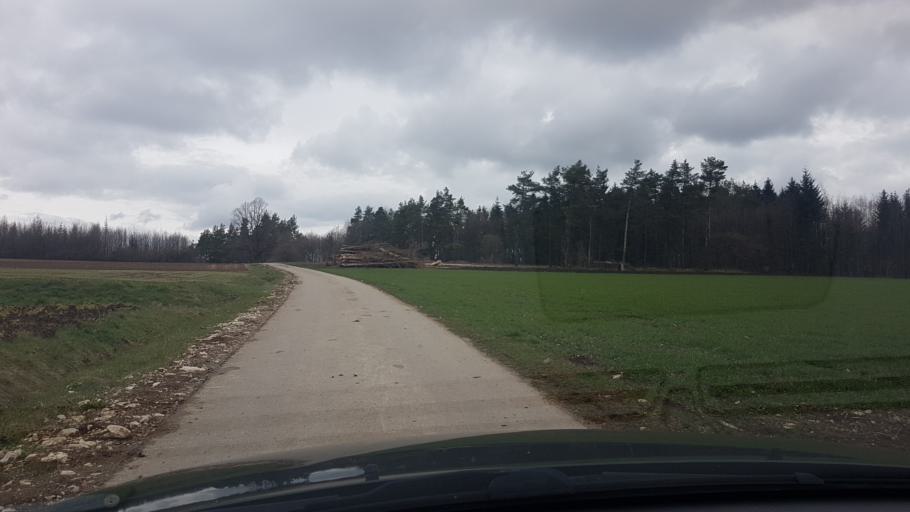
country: DE
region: Bavaria
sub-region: Upper Franconia
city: Heiligenstadt
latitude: 49.8623
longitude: 11.0954
